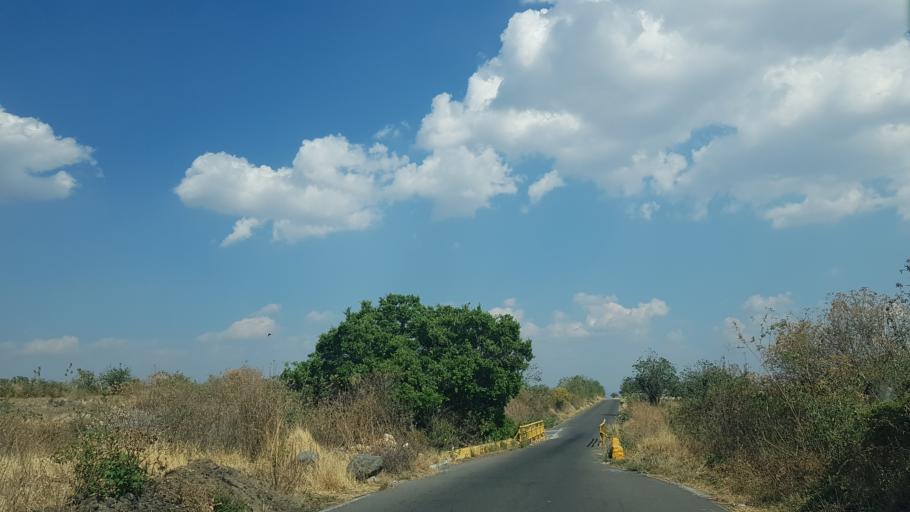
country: MX
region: Puebla
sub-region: Atlixco
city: Colonia Agricola de Ocotepec (Colonia San Jose)
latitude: 18.9210
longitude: -98.5335
